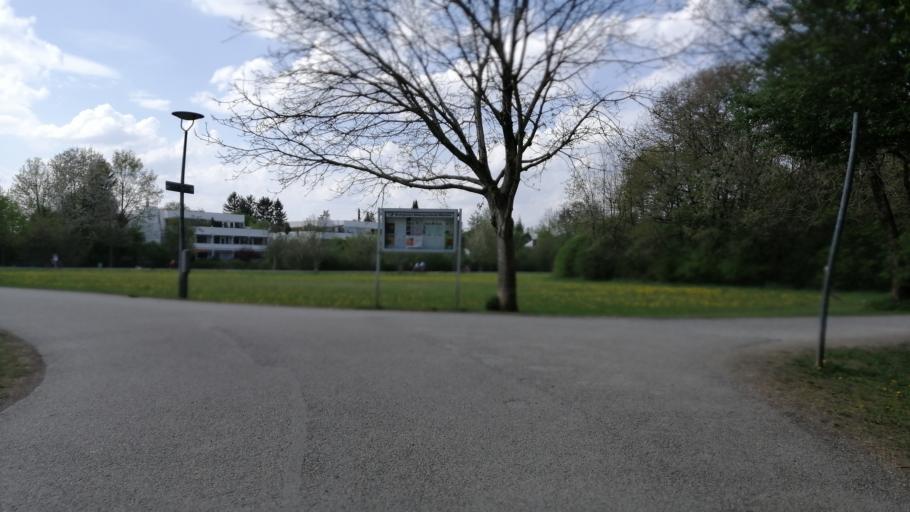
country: DE
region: Bavaria
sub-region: Upper Bavaria
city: Bogenhausen
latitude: 48.1500
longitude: 11.6349
